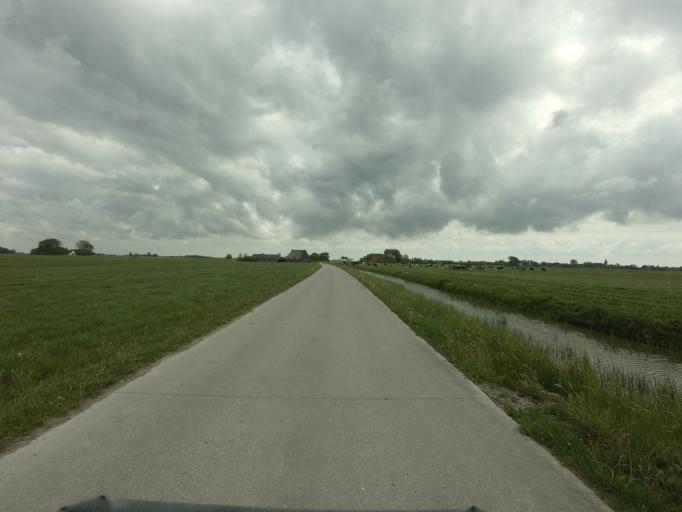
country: NL
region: Friesland
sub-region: Gemeente Littenseradiel
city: Wommels
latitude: 53.1087
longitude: 5.6156
